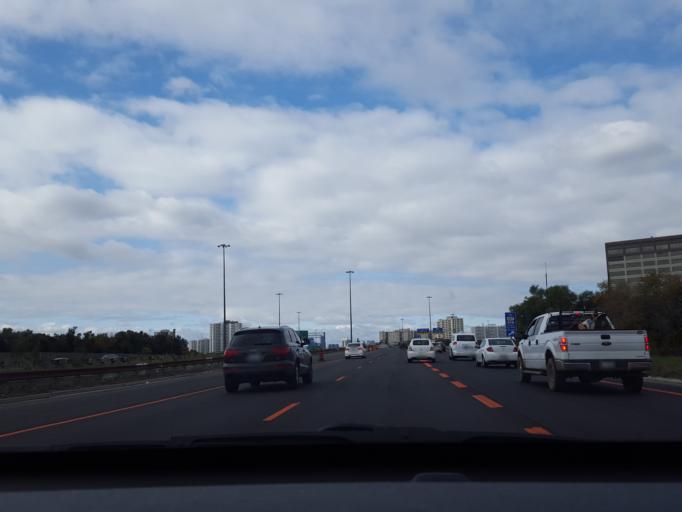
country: CA
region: Ontario
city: Scarborough
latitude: 43.7686
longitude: -79.3276
